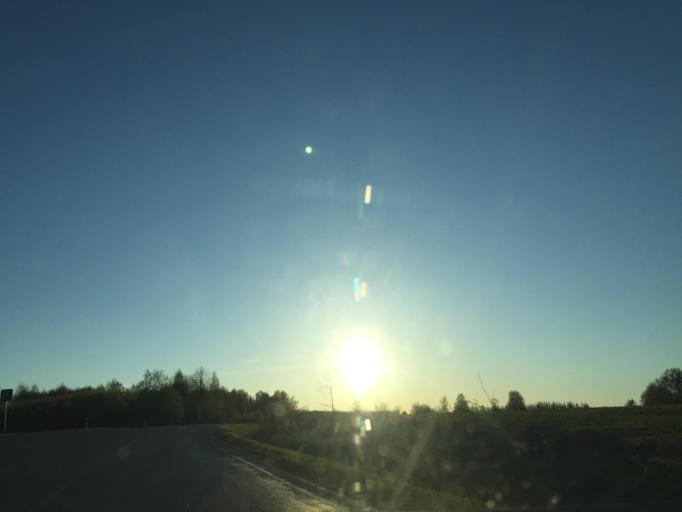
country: LV
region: Skriveri
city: Skriveri
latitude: 56.8861
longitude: 25.2004
